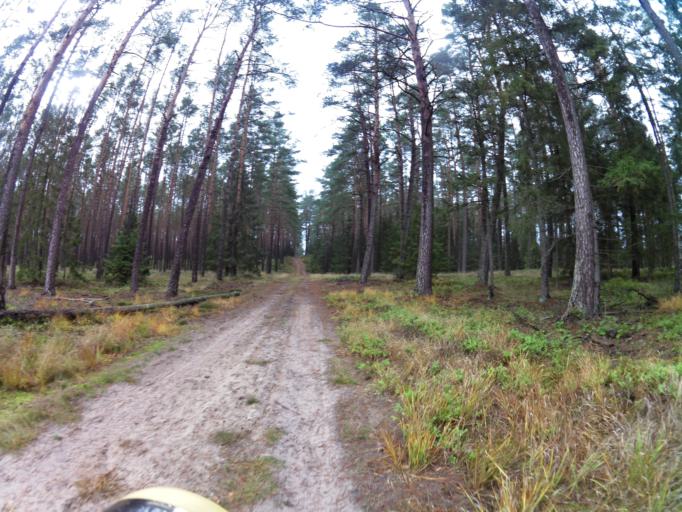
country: PL
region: West Pomeranian Voivodeship
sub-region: Powiat policki
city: Nowe Warpno
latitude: 53.6144
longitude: 14.3448
